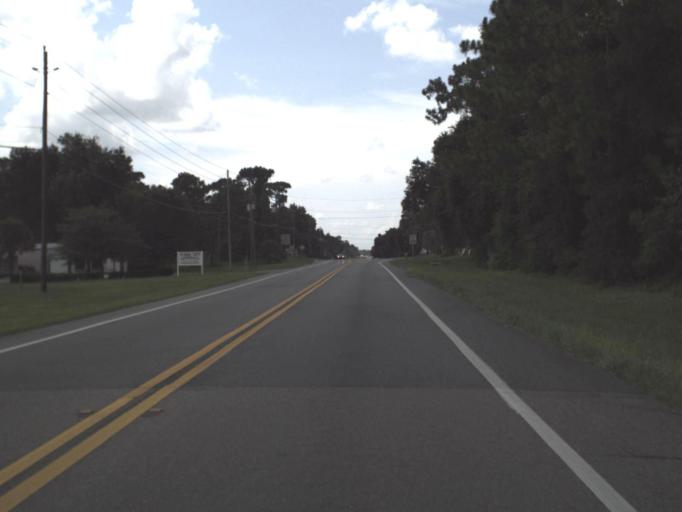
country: US
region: Florida
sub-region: Citrus County
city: Floral City
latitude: 28.7870
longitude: -82.3003
